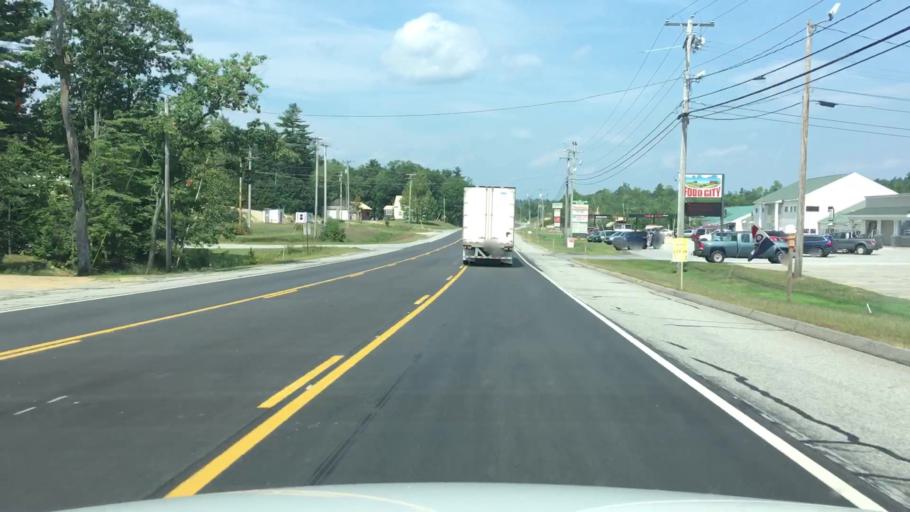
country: US
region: Maine
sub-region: Androscoggin County
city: Turner
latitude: 44.2683
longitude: -70.2676
